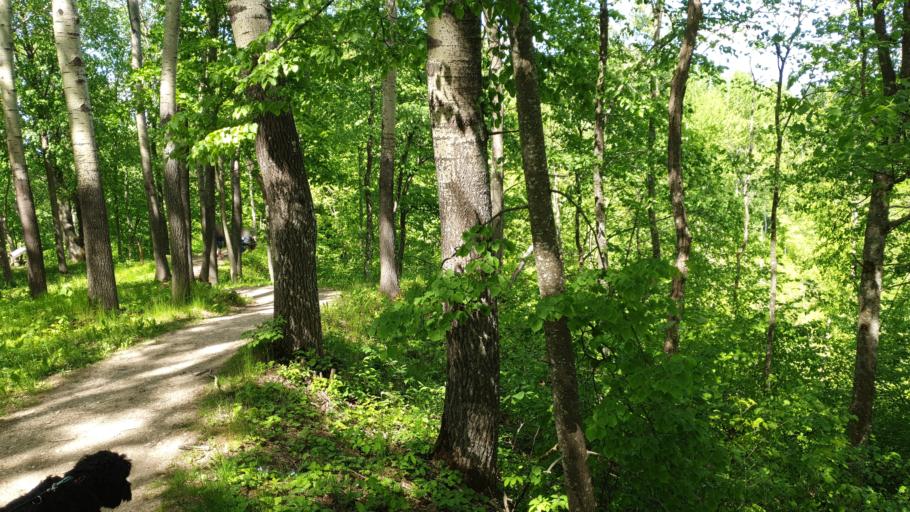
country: LT
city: Moletai
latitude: 55.0724
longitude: 25.4130
